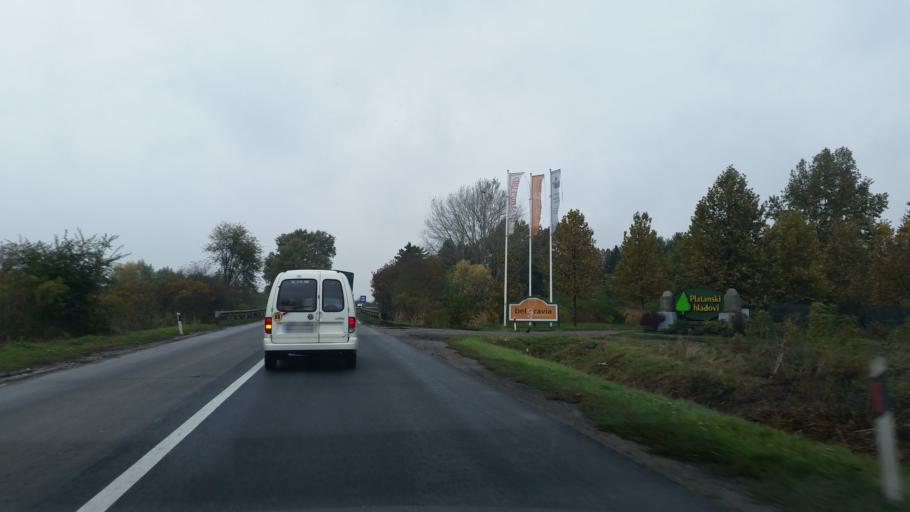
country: RS
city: Sefkerin
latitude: 44.9531
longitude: 20.4299
